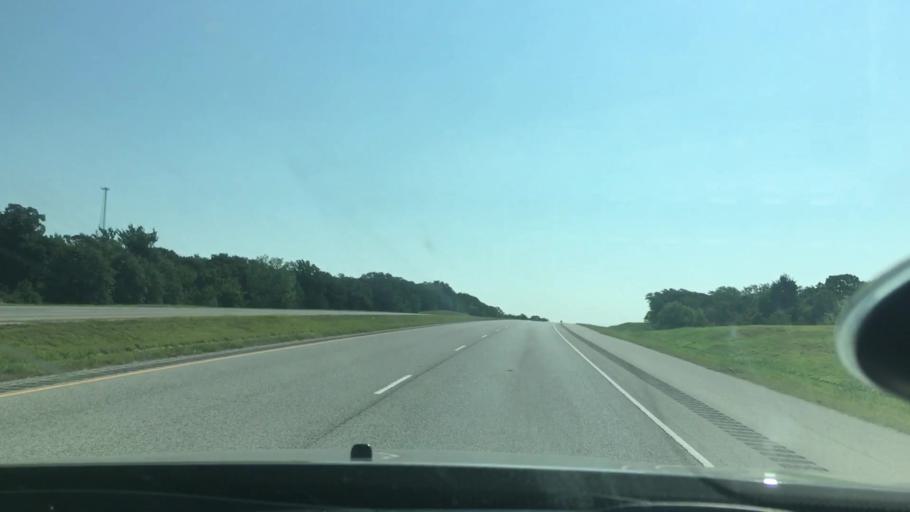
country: US
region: Oklahoma
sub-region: Carter County
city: Dickson
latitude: 34.1126
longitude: -97.0084
